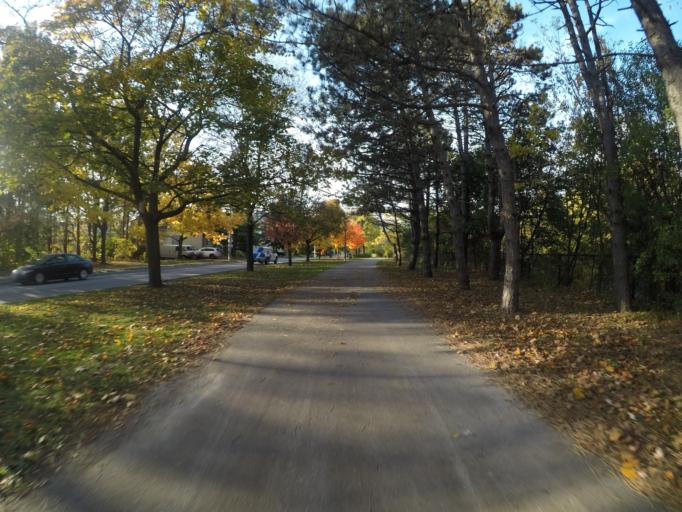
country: CA
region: Ontario
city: Kitchener
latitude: 43.4421
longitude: -80.4923
